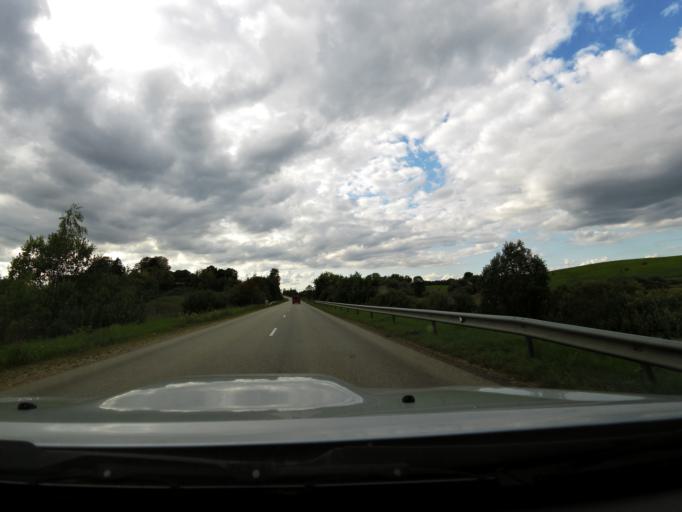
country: LV
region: Ilukste
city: Ilukste
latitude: 55.9769
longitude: 26.0137
